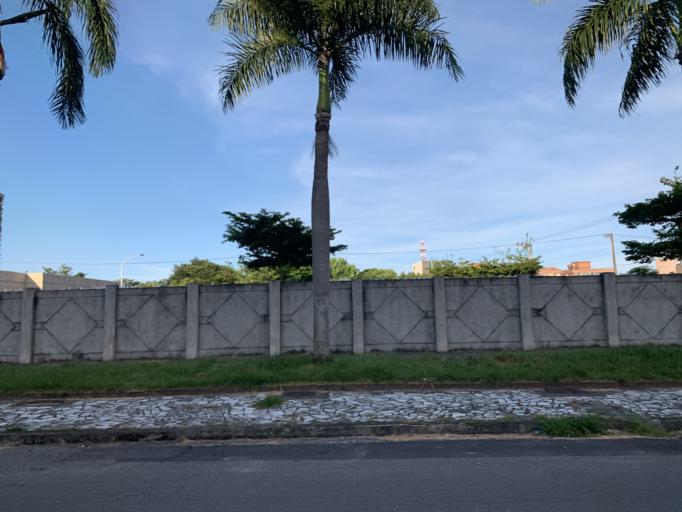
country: TW
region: Taiwan
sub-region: Hualien
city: Hualian
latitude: 24.0019
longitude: 121.6293
